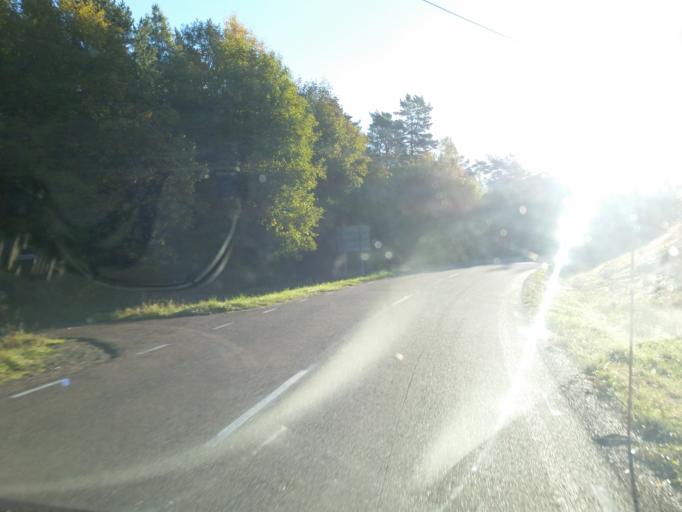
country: AX
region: Alands skaergard
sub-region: Vardoe
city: Vardoe
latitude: 60.2273
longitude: 20.4086
